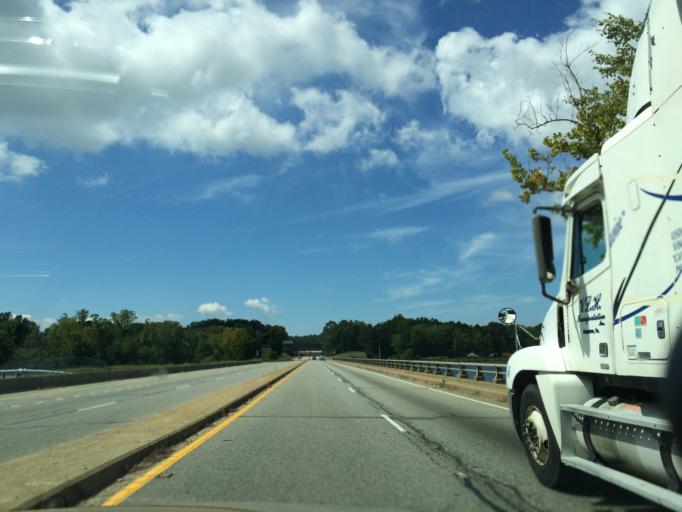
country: US
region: Virginia
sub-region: York County
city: Yorktown
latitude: 37.1728
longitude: -76.5609
